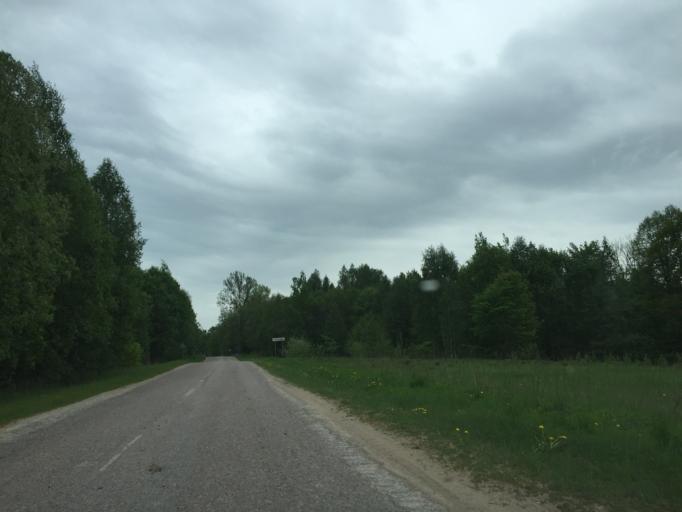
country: LV
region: Lielvarde
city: Lielvarde
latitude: 56.8030
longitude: 24.8633
